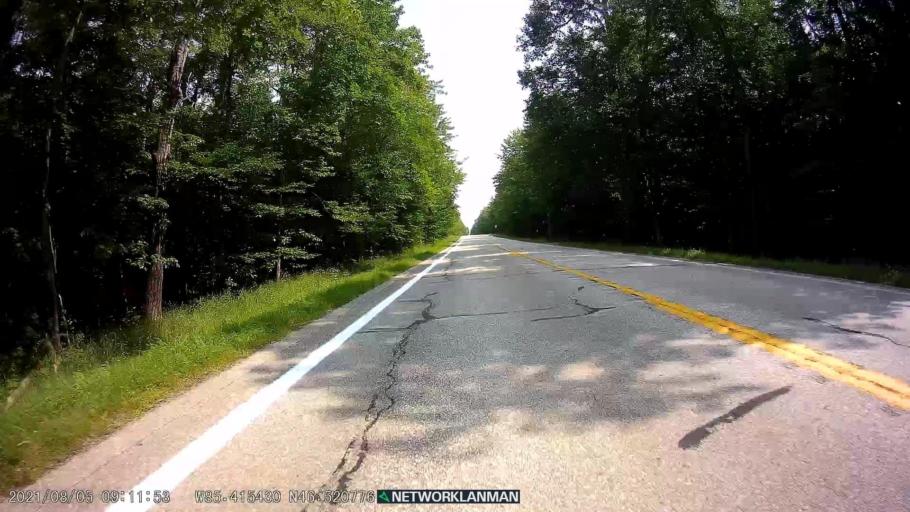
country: US
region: Michigan
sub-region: Luce County
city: Newberry
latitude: 46.5206
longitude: -85.4158
